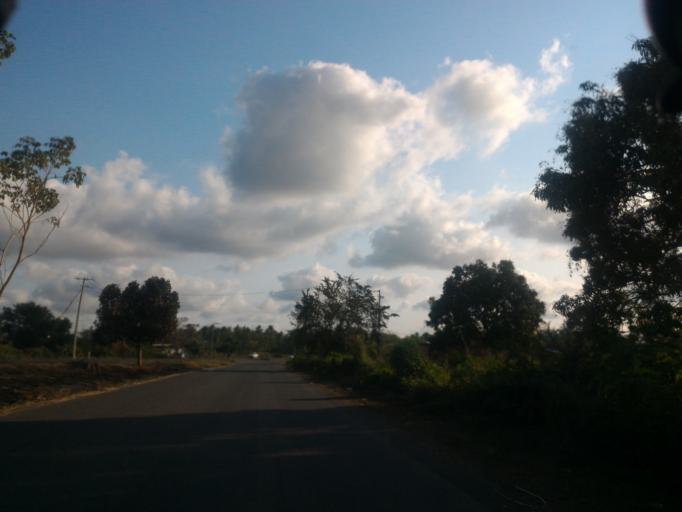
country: MX
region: Colima
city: Tecoman
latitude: 18.9107
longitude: -103.8542
